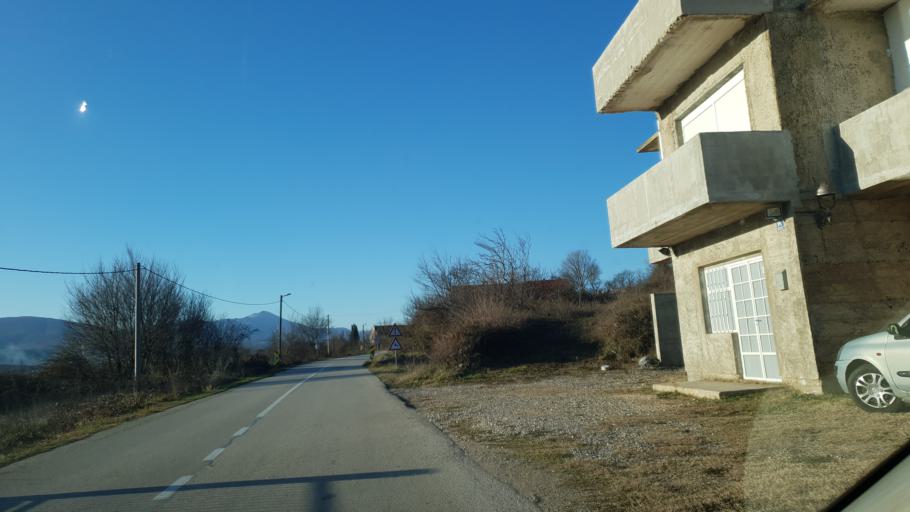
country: HR
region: Splitsko-Dalmatinska
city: Gala
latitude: 43.7331
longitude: 16.6885
